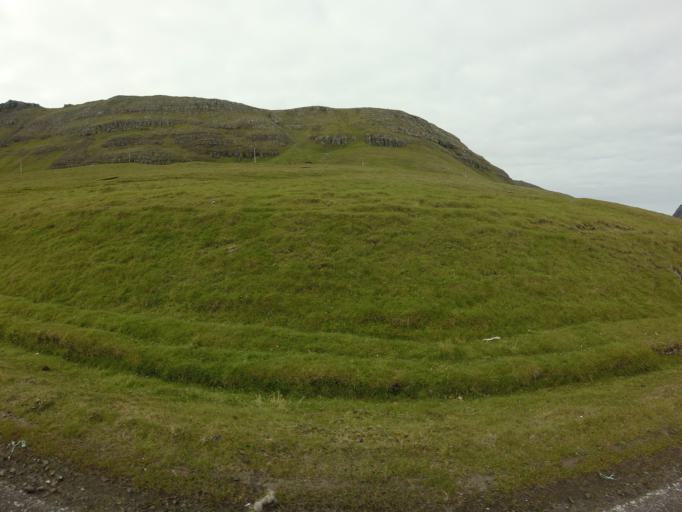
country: FO
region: Suduroy
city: Tvoroyri
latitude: 61.5923
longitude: -6.9473
